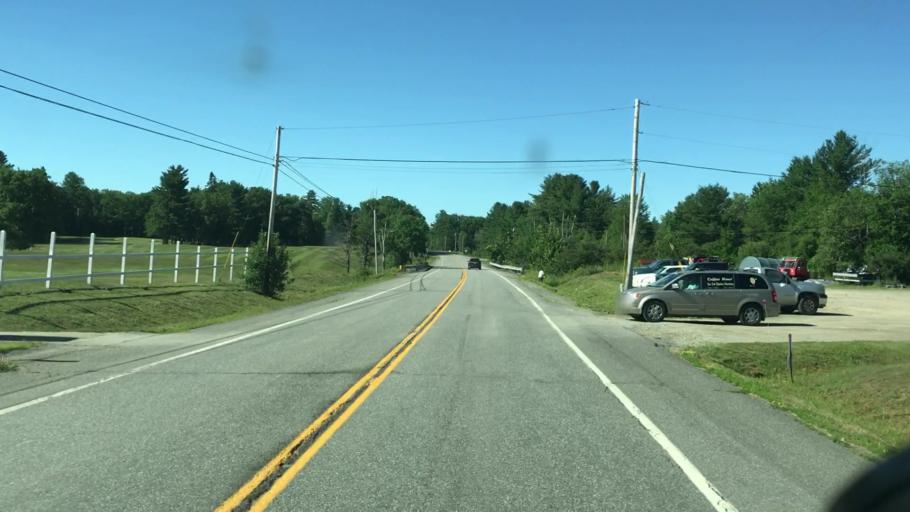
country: US
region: Maine
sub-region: Penobscot County
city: Enfield
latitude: 45.2973
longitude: -68.6195
